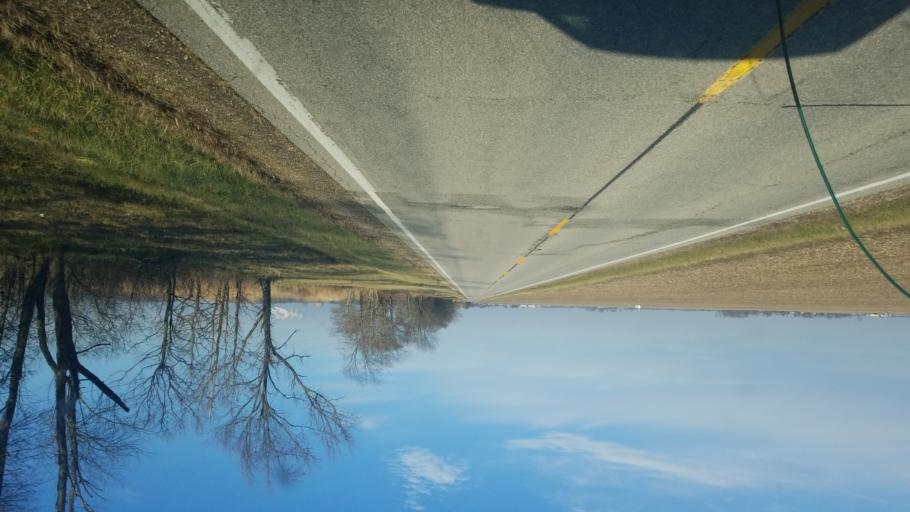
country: US
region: Illinois
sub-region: Edwards County
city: Grayville
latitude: 38.3296
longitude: -87.9061
